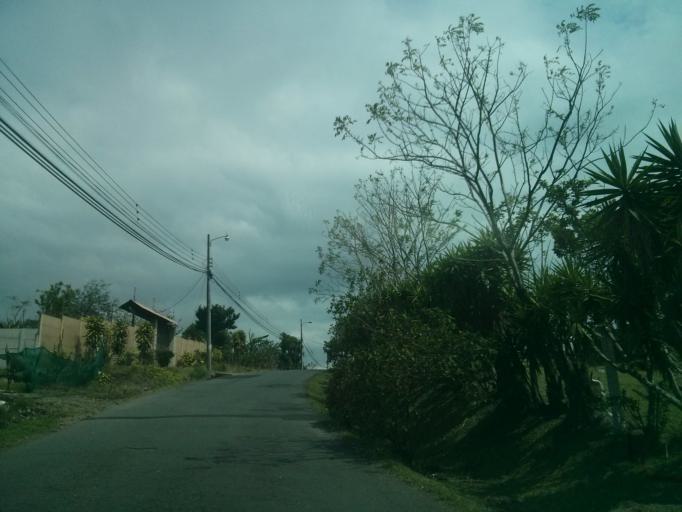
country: CR
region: Heredia
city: Angeles
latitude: 10.0095
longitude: -84.0328
